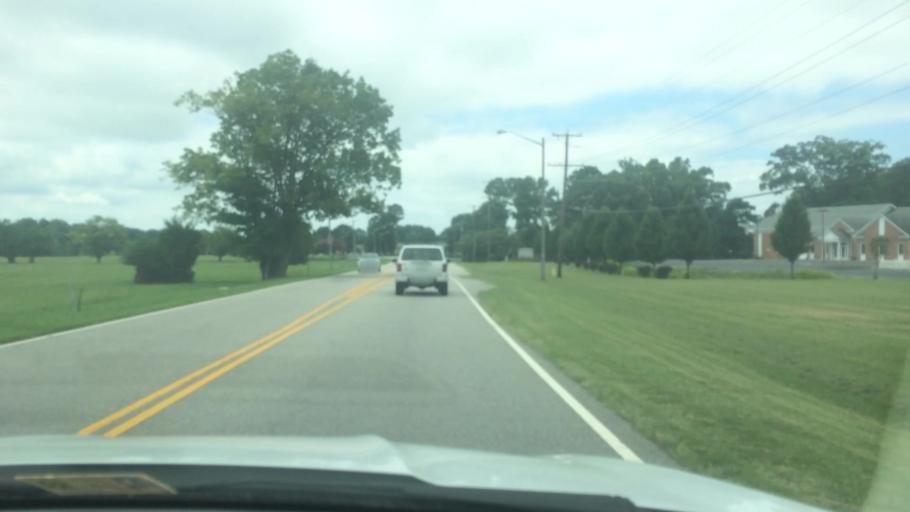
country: US
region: Virginia
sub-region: York County
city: Yorktown
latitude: 37.2139
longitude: -76.5704
